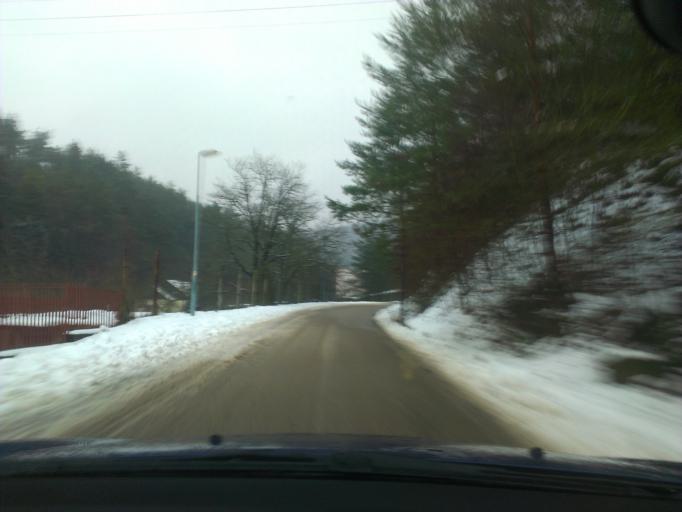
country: SK
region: Trnavsky
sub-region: Okres Trnava
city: Piestany
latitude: 48.5771
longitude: 17.8578
